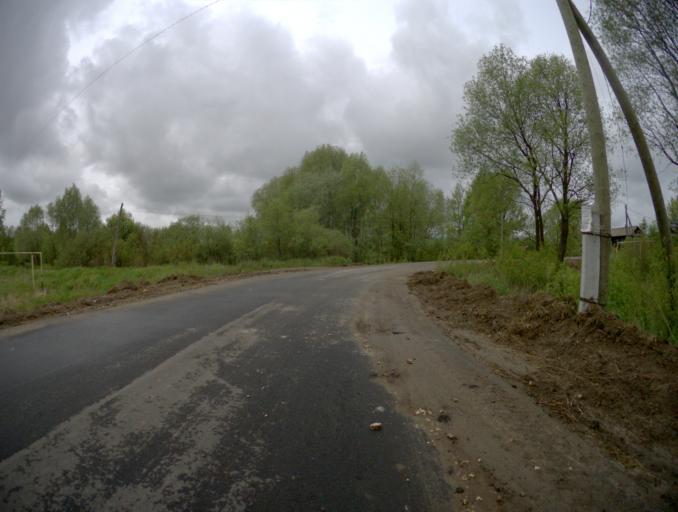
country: RU
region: Rjazan
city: Gus'-Zheleznyy
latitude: 55.2378
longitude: 41.0474
